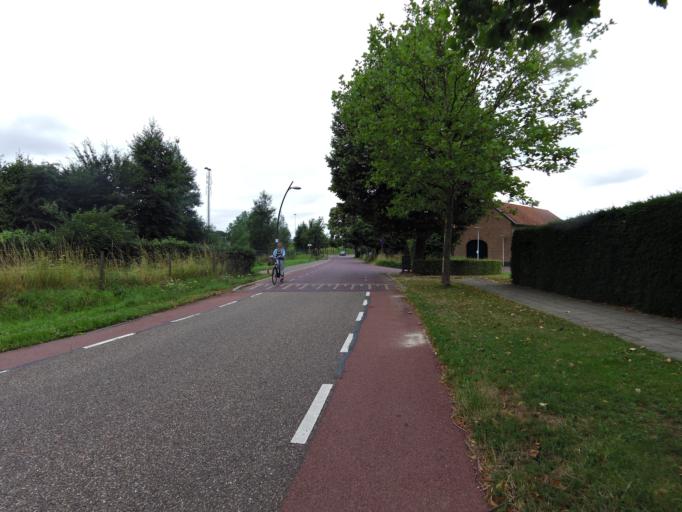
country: NL
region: Limburg
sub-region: Gemeente Nuth
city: Nuth
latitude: 50.9119
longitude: 5.8882
